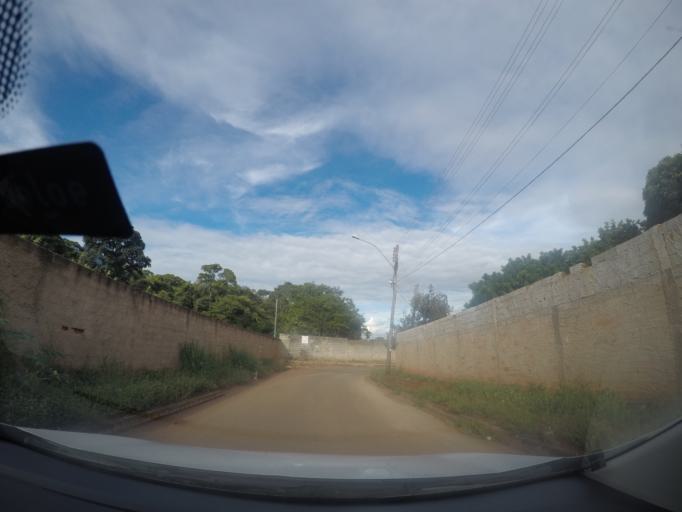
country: BR
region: Goias
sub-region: Goiania
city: Goiania
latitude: -16.6311
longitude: -49.3518
